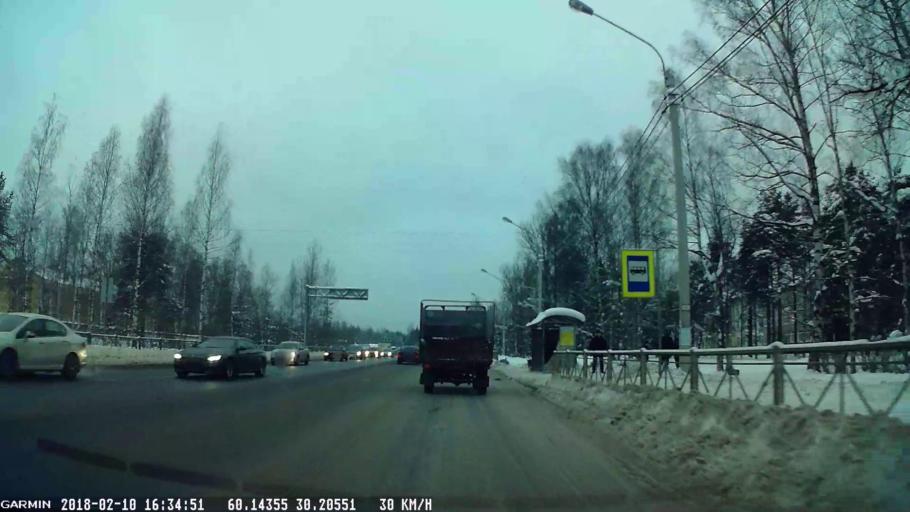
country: RU
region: Leningrad
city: Sertolovo
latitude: 60.1442
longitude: 30.2048
